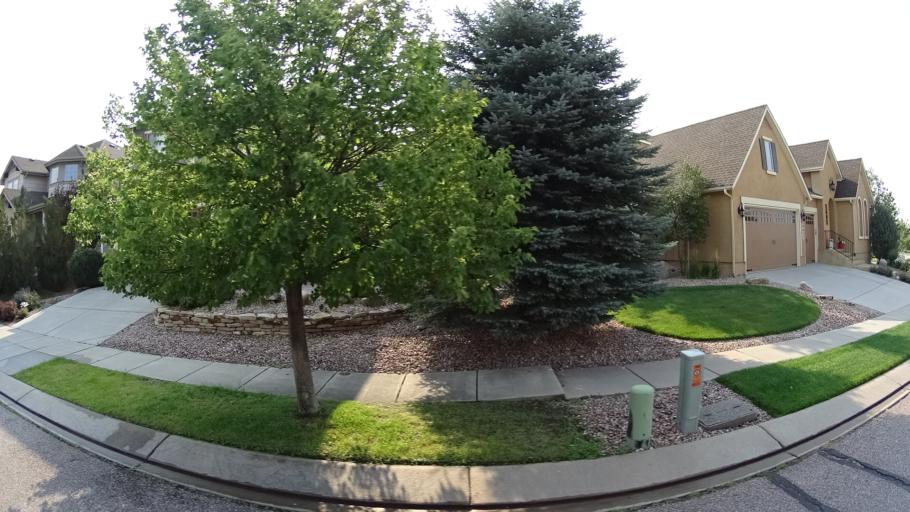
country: US
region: Colorado
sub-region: El Paso County
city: Black Forest
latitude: 38.9562
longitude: -104.7226
